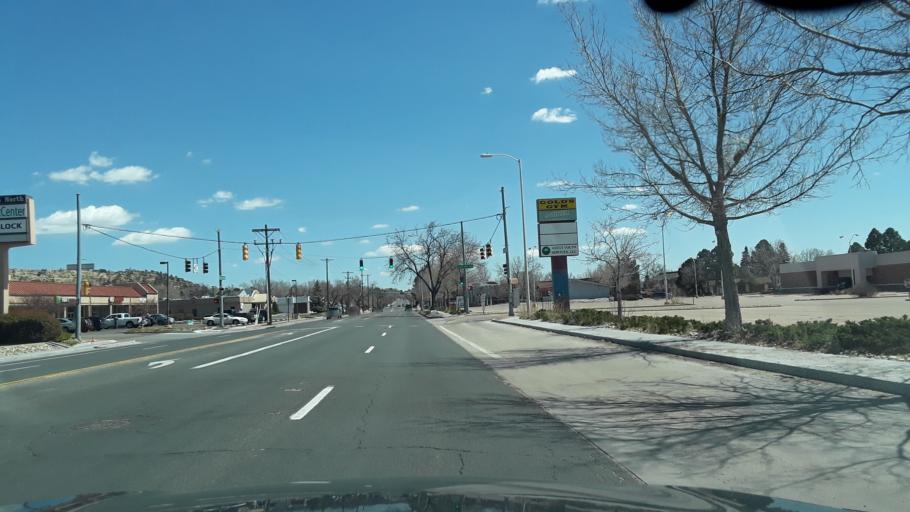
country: US
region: Colorado
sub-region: El Paso County
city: Cimarron Hills
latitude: 38.8543
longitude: -104.7551
